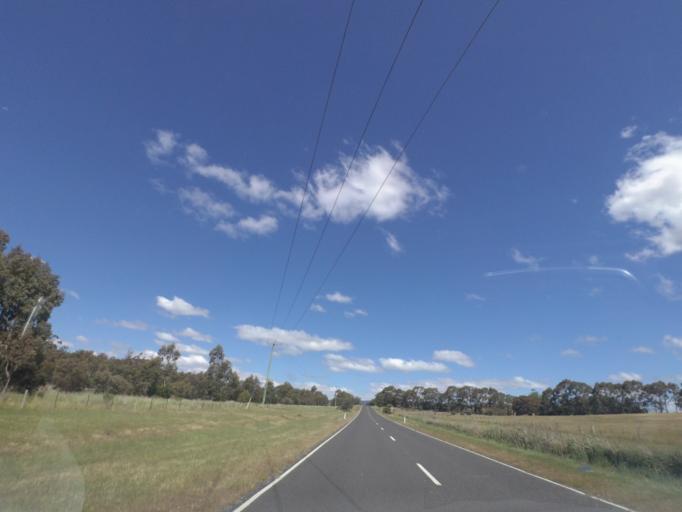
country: AU
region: Victoria
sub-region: Hume
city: Sunbury
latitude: -37.2987
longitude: 144.5068
